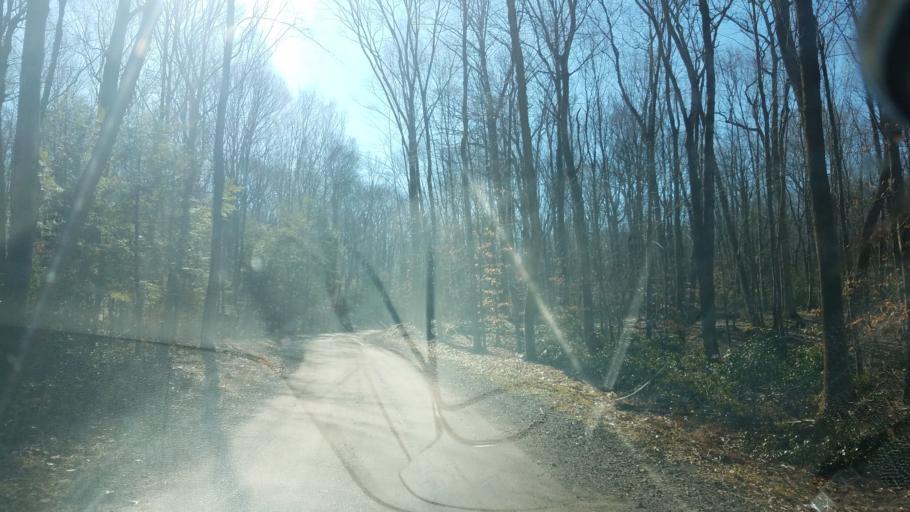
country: US
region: Connecticut
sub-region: New Haven County
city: Heritage Village
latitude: 41.5134
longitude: -73.2836
